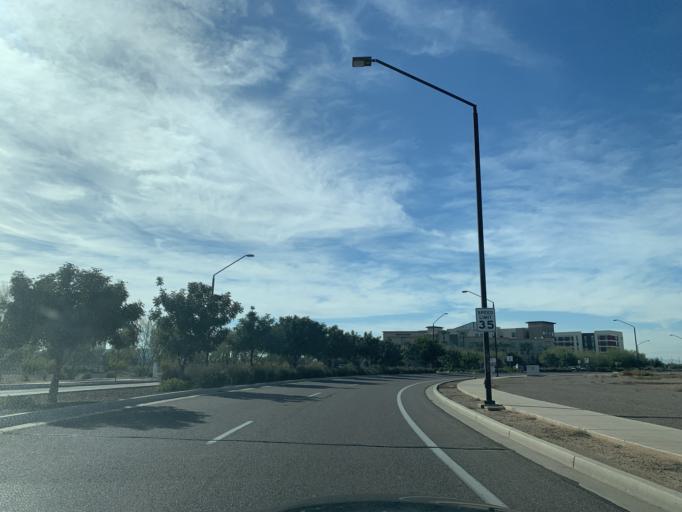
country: US
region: Arizona
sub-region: Maricopa County
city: Gilbert
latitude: 33.2928
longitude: -111.7502
